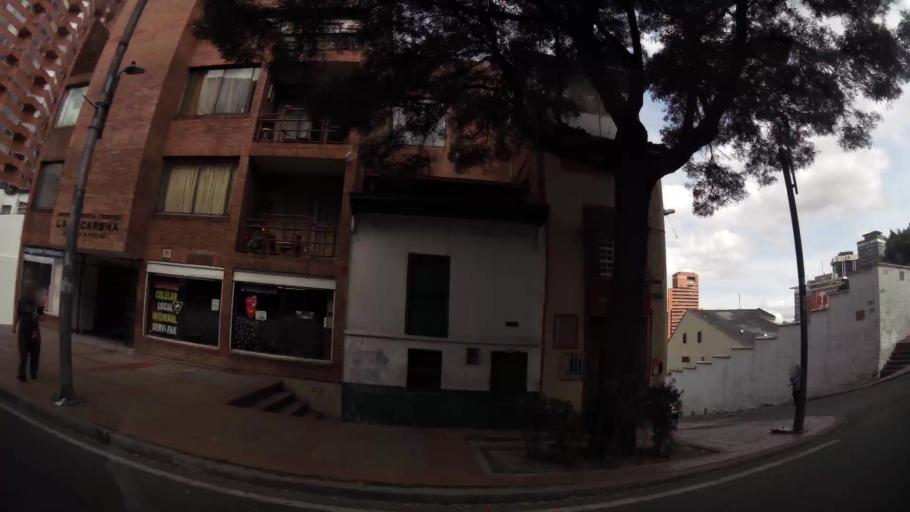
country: CO
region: Bogota D.C.
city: Bogota
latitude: 4.6113
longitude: -74.0666
